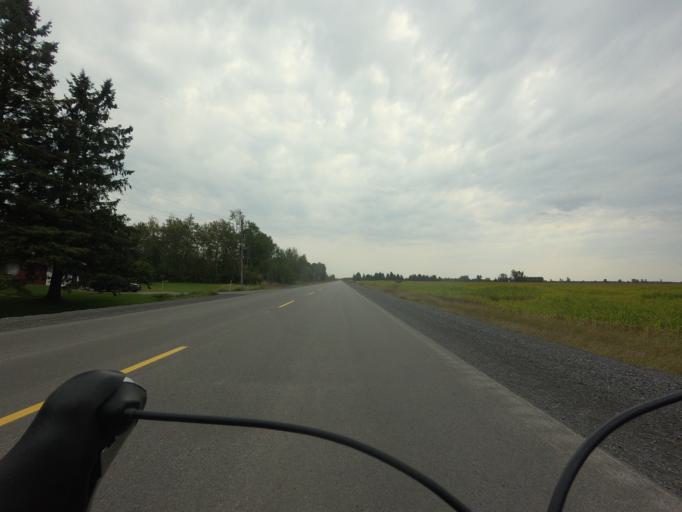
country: CA
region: Ontario
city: Bells Corners
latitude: 45.2130
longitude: -75.7701
